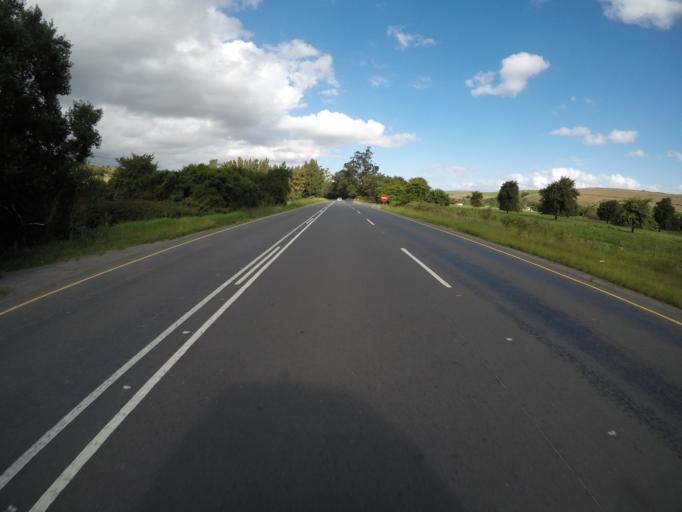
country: ZA
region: Western Cape
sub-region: Overberg District Municipality
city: Swellendam
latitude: -34.0027
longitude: 20.3730
